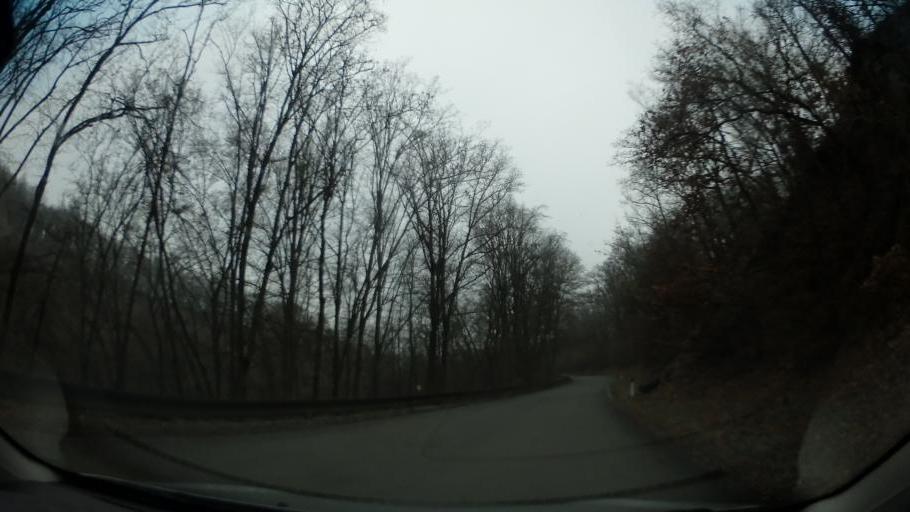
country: CZ
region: Vysocina
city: Mohelno
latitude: 49.1401
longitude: 16.2071
